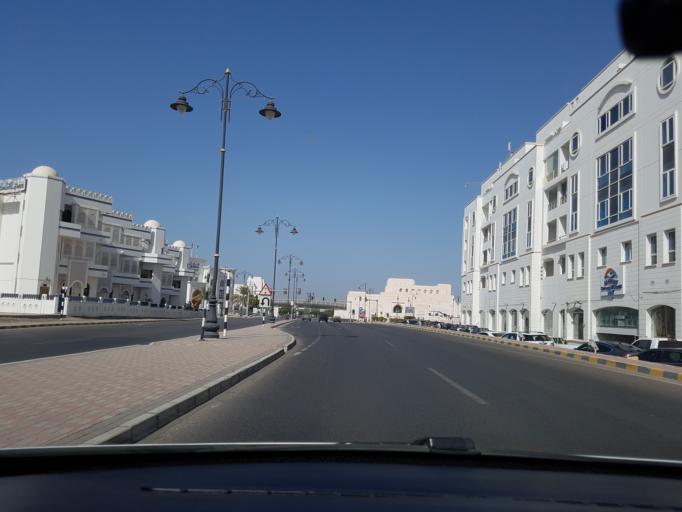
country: OM
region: Muhafazat Masqat
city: Bawshar
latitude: 23.6128
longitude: 58.4644
